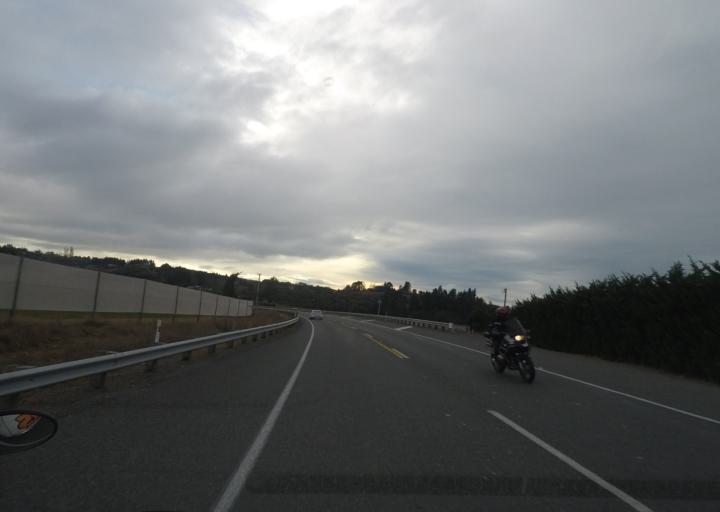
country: NZ
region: Tasman
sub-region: Tasman District
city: Mapua
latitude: -41.2576
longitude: 173.0727
